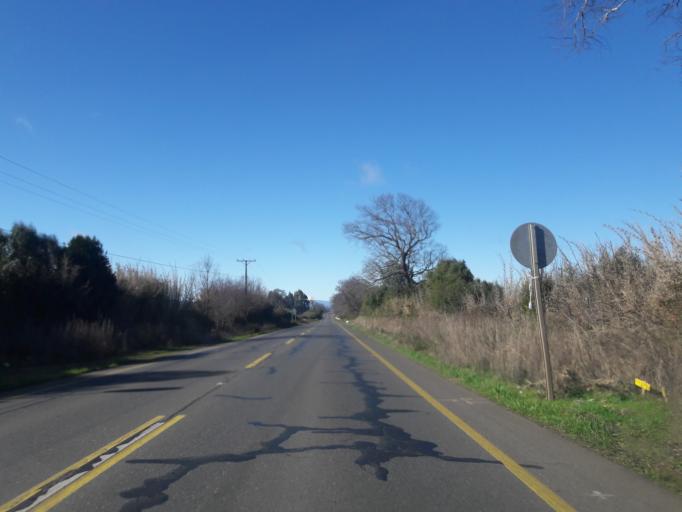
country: CL
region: Araucania
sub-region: Provincia de Malleco
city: Victoria
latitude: -38.2540
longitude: -72.2795
